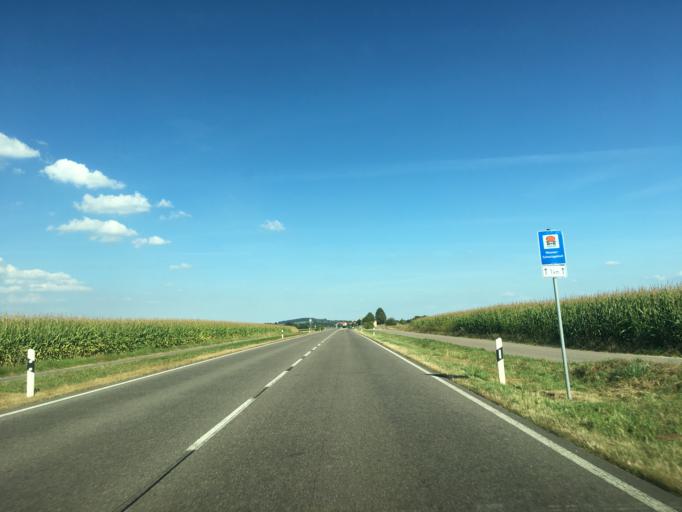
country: DE
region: Baden-Wuerttemberg
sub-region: Tuebingen Region
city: Obermarchtal
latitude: 48.2337
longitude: 9.5797
